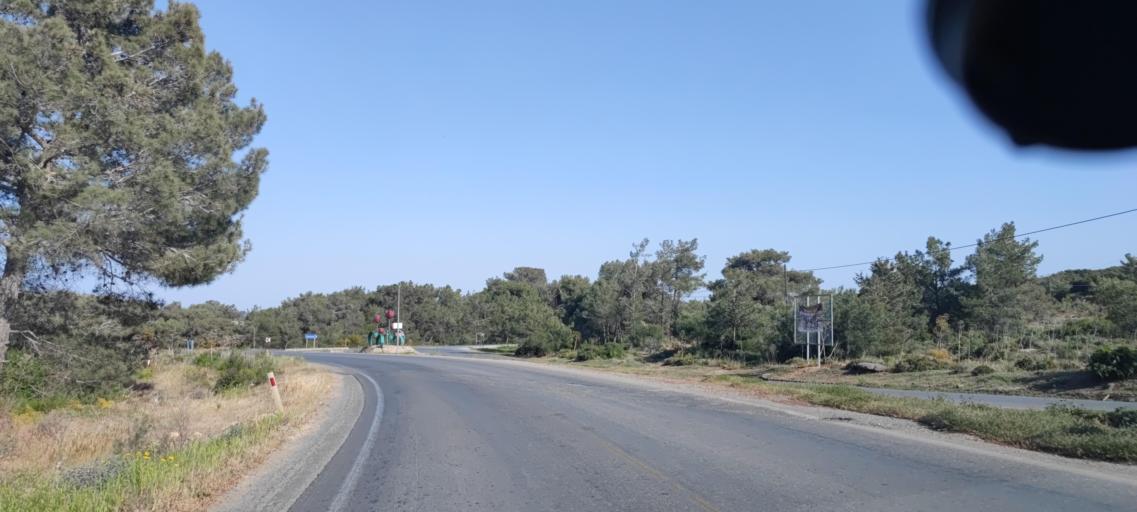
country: CY
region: Keryneia
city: Lapithos
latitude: 35.3094
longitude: 33.0606
